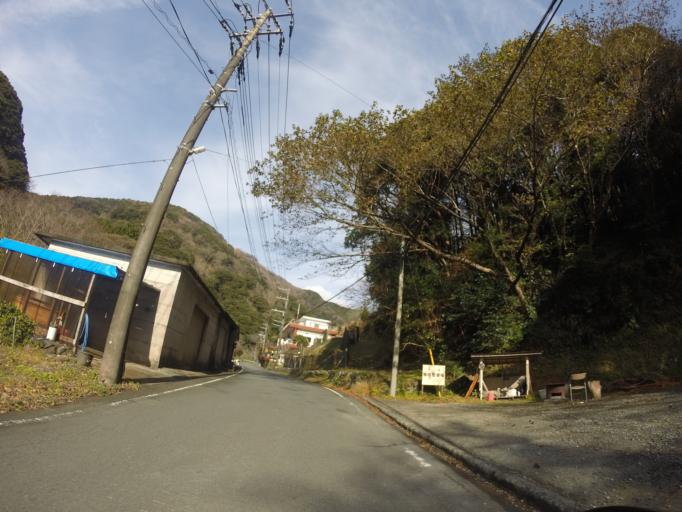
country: JP
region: Shizuoka
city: Heda
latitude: 34.8145
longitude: 138.8261
